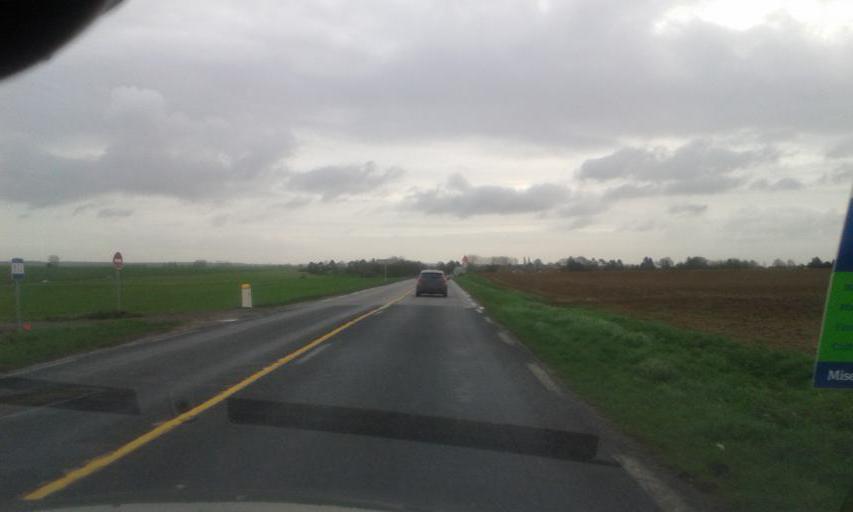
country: FR
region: Haute-Normandie
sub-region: Departement de l'Eure
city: Pont-Saint-Pierre
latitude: 49.3884
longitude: 1.2909
